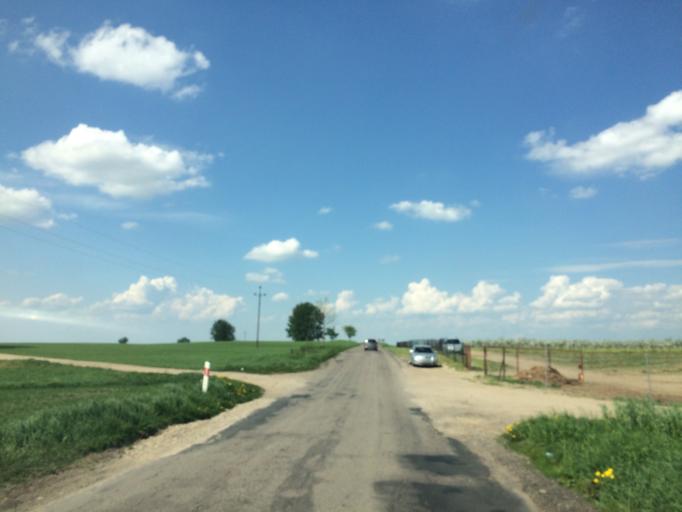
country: PL
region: Warmian-Masurian Voivodeship
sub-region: Powiat dzialdowski
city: Rybno
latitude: 53.3999
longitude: 19.8594
